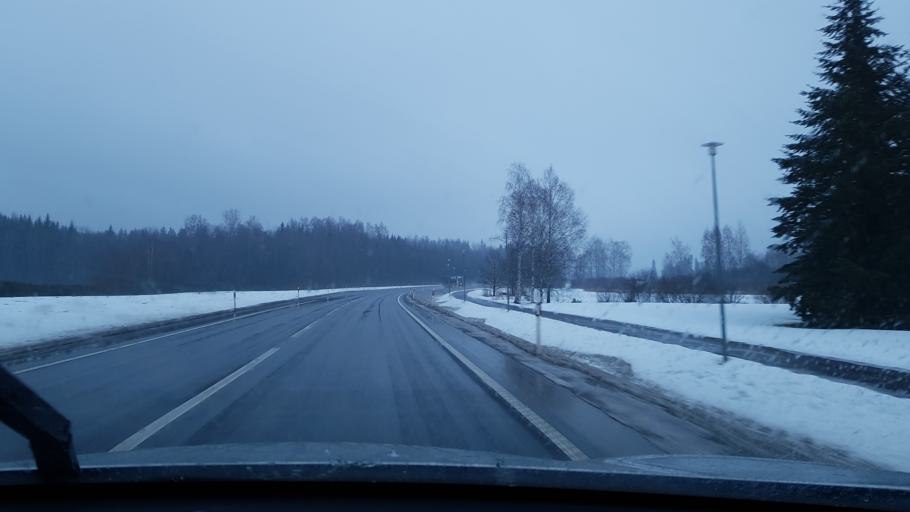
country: EE
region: Jaervamaa
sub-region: Tueri vald
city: Tueri
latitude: 58.8283
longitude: 25.4595
